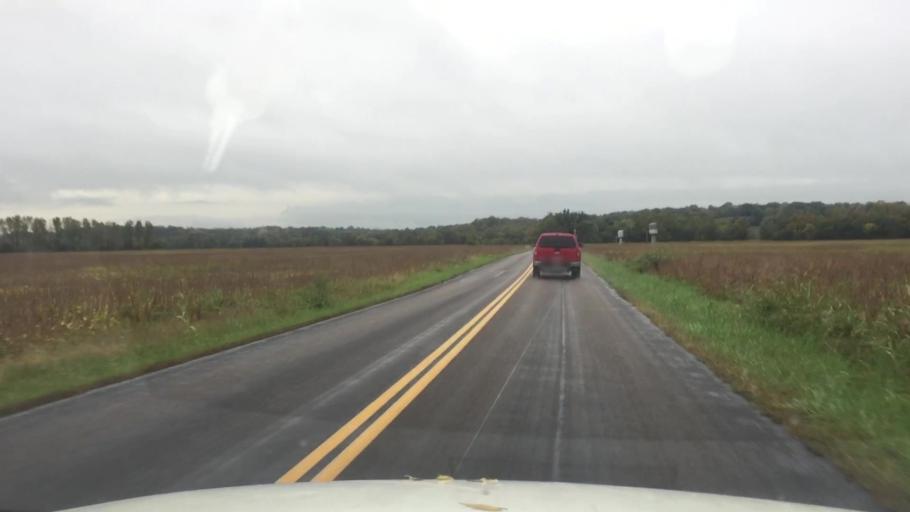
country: US
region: Missouri
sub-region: Boone County
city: Columbia
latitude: 38.8935
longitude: -92.4649
